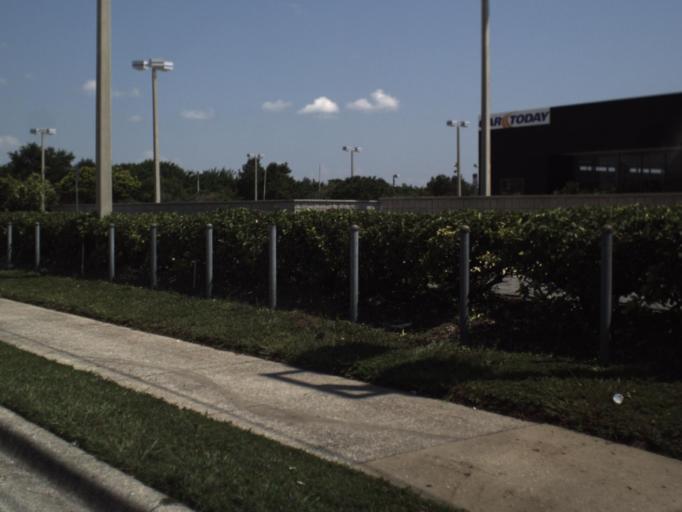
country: US
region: Florida
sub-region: Pinellas County
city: Bay Pines
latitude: 27.8391
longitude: -82.7550
